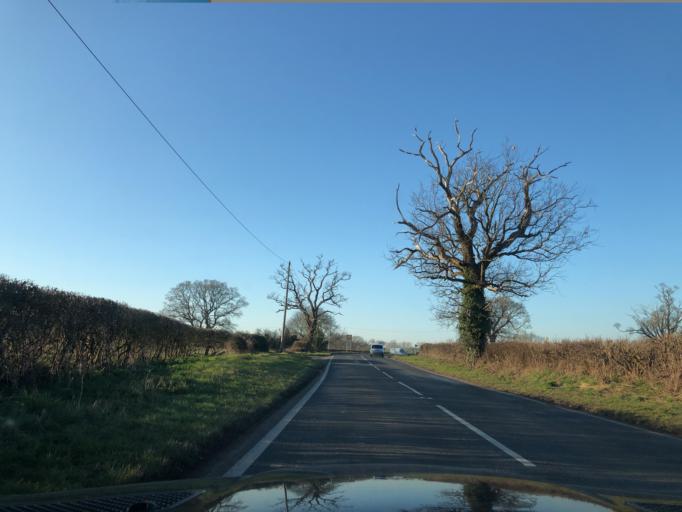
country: GB
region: England
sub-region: Warwickshire
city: Warwick
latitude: 52.2703
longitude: -1.6330
